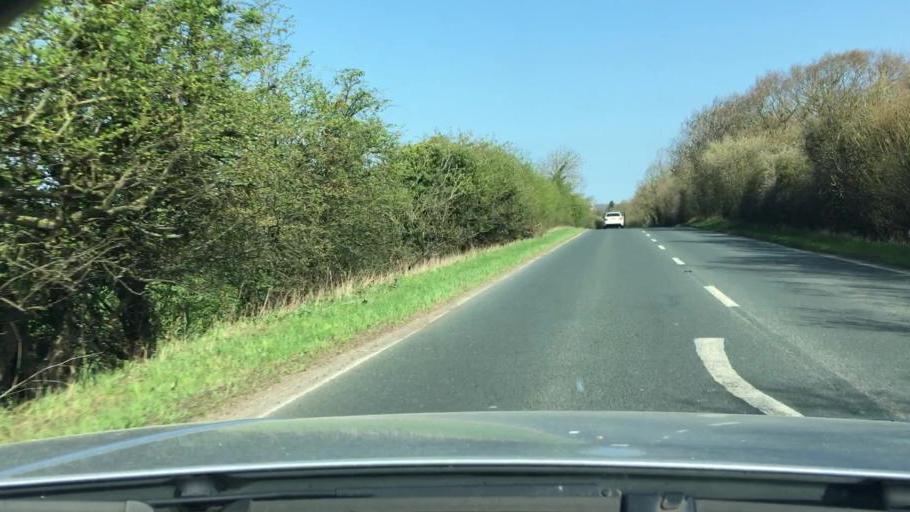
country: GB
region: England
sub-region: North Yorkshire
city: Pannal
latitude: 53.9423
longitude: -1.5381
